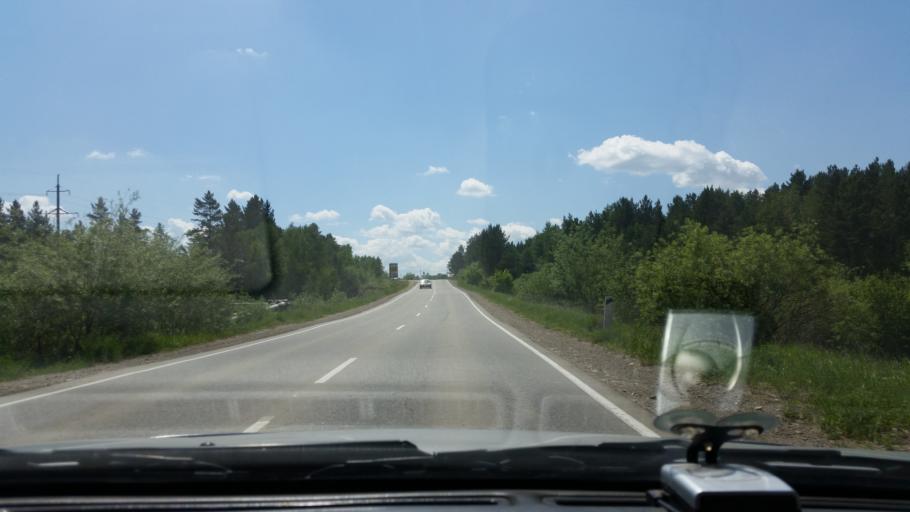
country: RU
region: Irkutsk
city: Smolenshchina
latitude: 52.2295
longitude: 104.2013
